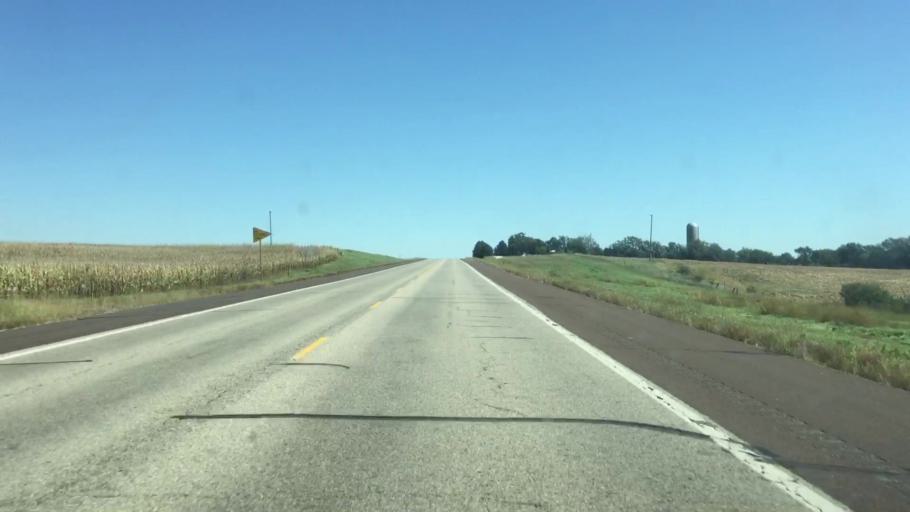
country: US
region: Kansas
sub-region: Nemaha County
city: Seneca
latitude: 39.8421
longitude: -96.3030
